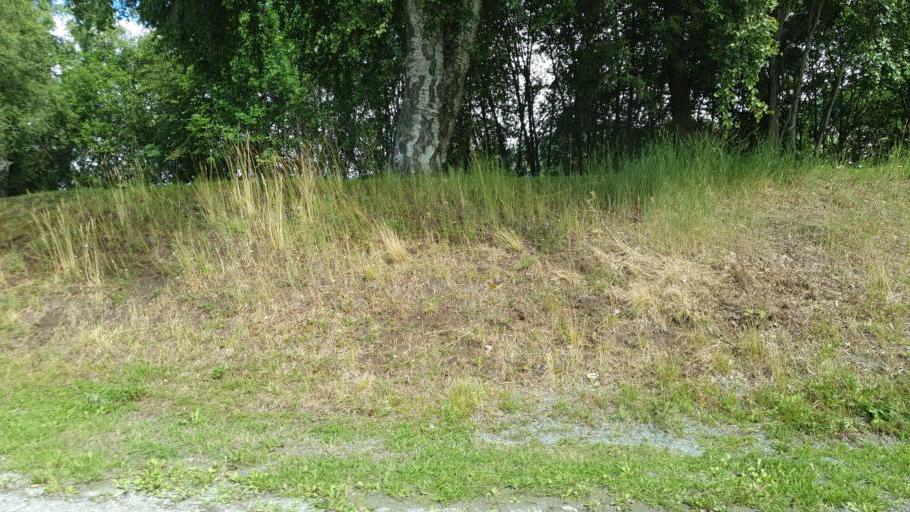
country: NO
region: Sor-Trondelag
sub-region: Midtre Gauldal
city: Storen
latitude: 63.0315
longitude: 10.2935
